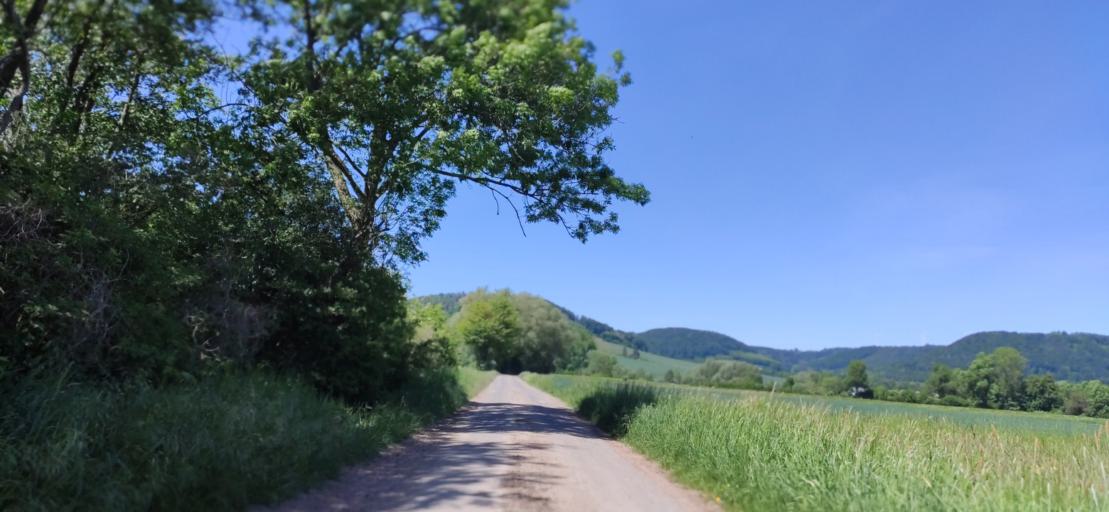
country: DE
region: Lower Saxony
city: Boffzen
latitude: 51.7223
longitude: 9.3663
